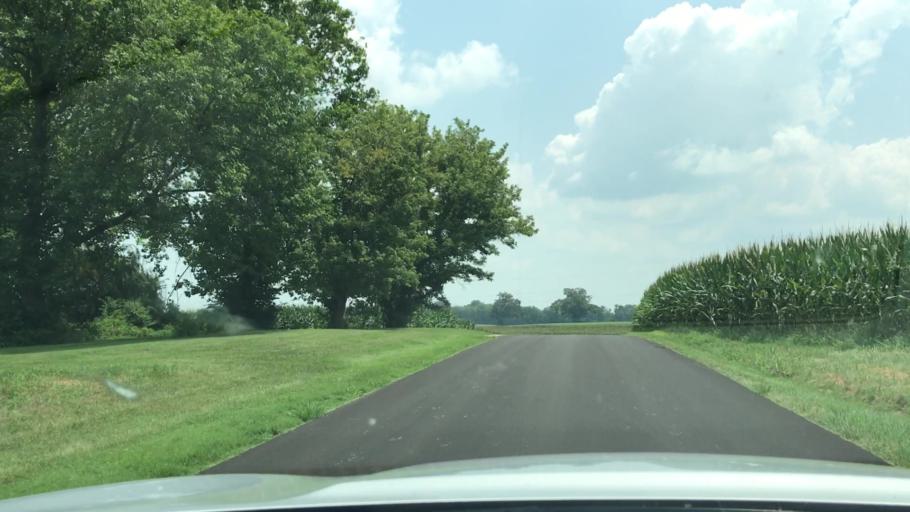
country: US
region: Kentucky
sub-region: Todd County
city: Elkton
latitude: 36.7780
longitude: -87.1466
